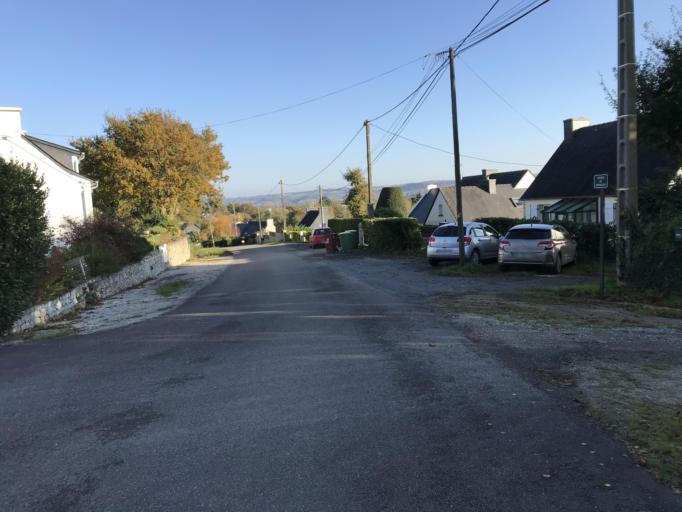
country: FR
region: Brittany
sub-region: Departement du Finistere
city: Hopital-Camfrout
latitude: 48.2987
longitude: -4.2275
